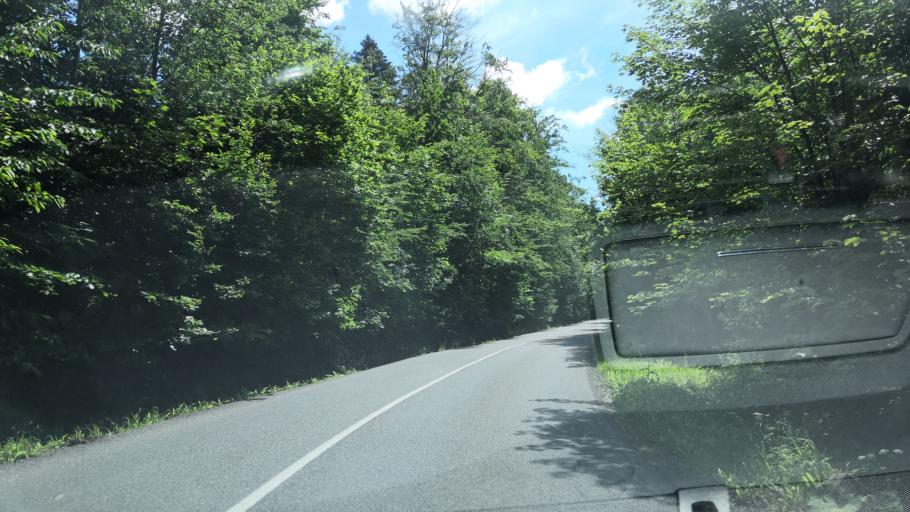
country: CZ
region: Zlin
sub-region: Okres Vsetin
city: Roznov pod Radhostem
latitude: 49.4351
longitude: 18.1317
